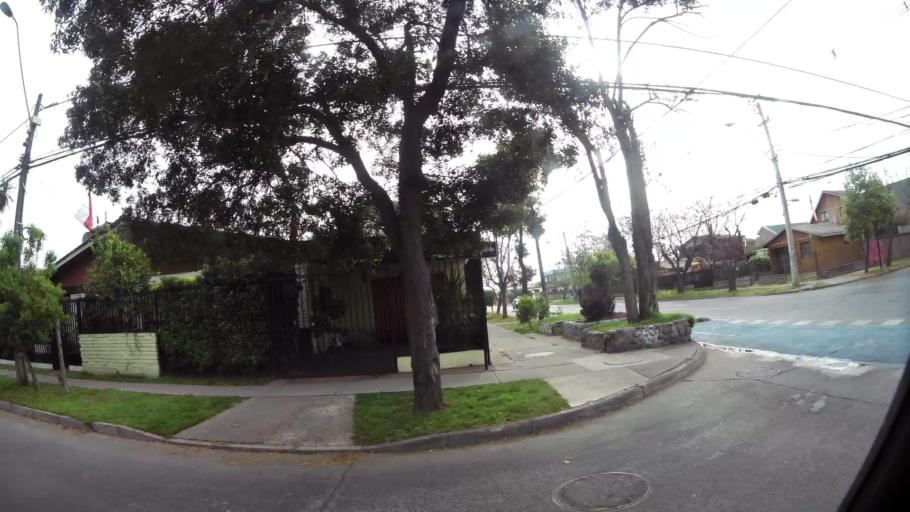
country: CL
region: Santiago Metropolitan
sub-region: Provincia de Santiago
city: Lo Prado
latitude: -33.5215
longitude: -70.7723
